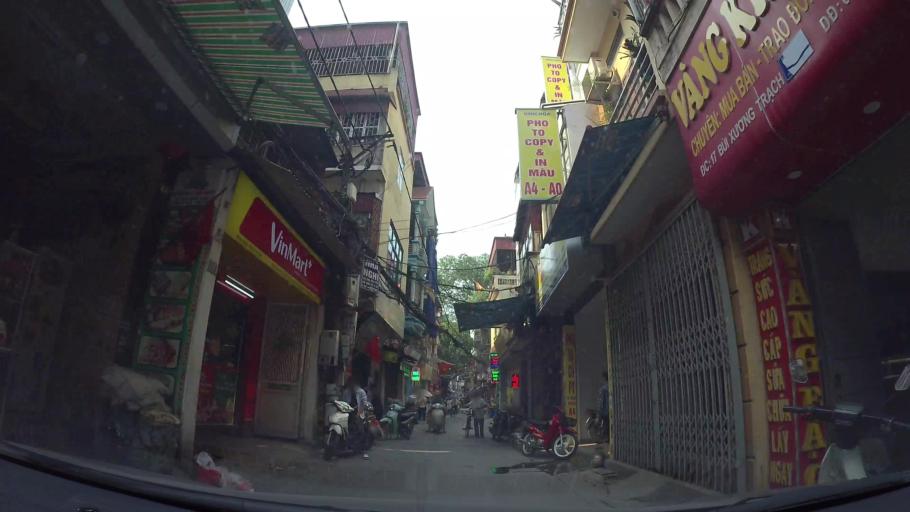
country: VN
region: Ha Noi
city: Thanh Xuan
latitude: 20.9915
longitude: 105.8173
